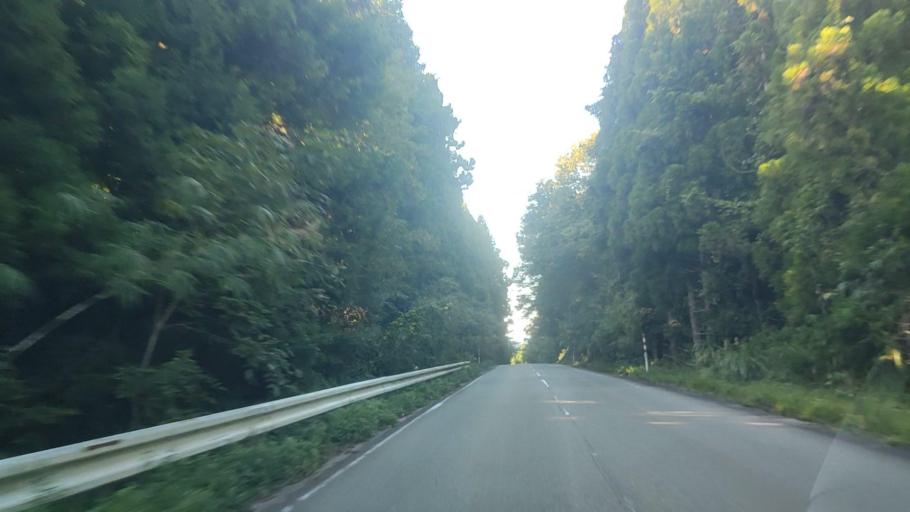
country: JP
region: Ishikawa
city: Nanao
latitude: 37.1217
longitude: 136.9359
